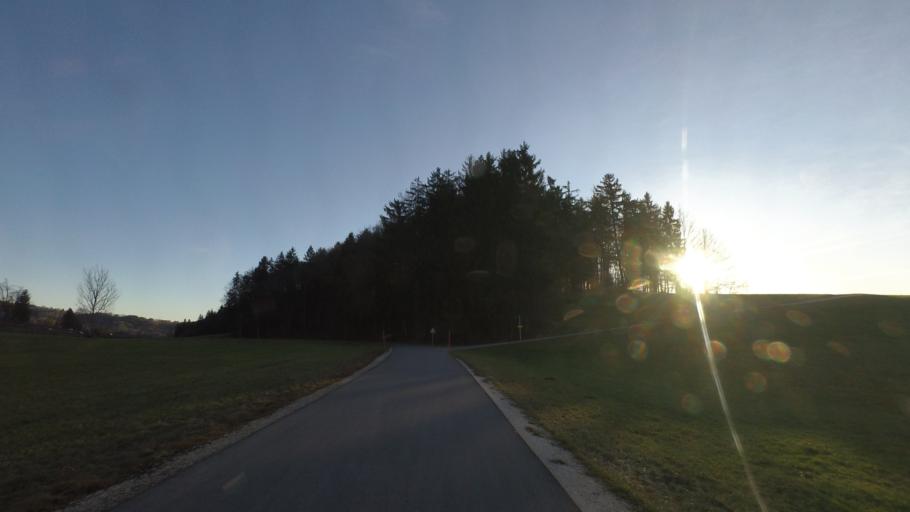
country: DE
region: Bavaria
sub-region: Upper Bavaria
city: Vachendorf
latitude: 47.8269
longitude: 12.6188
